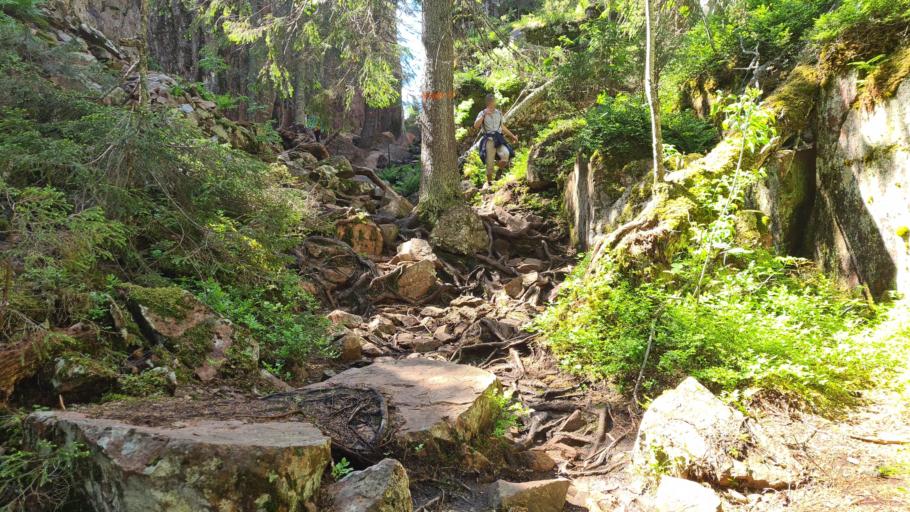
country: SE
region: Vaesternorrland
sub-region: OErnskoeldsviks Kommun
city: Kopmanholmen
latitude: 63.1089
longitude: 18.5022
